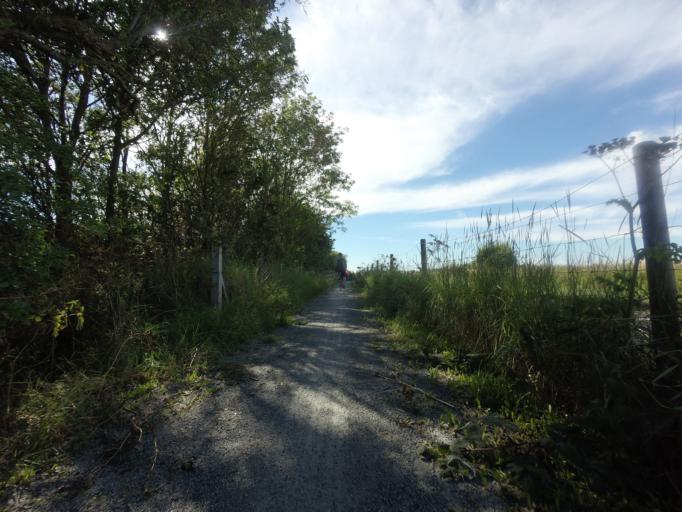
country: GB
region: England
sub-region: Kent
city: Herne Bay
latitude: 51.3628
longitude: 1.2163
